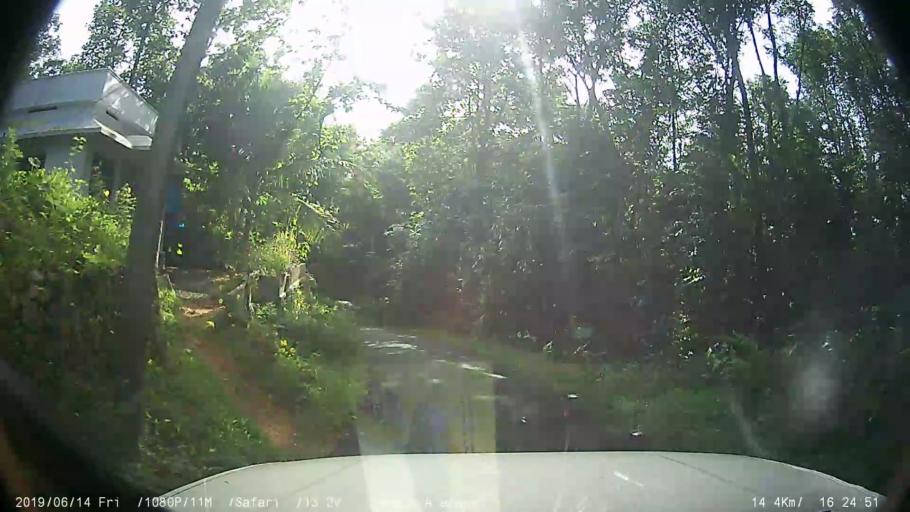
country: IN
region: Kerala
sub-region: Kottayam
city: Palackattumala
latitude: 9.7753
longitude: 76.5974
